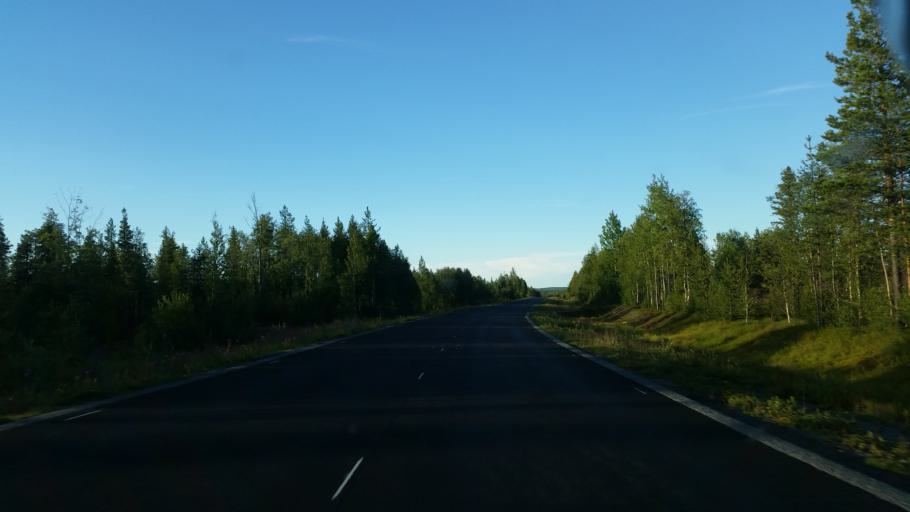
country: SE
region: Vaesterbotten
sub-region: Dorotea Kommun
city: Dorotea
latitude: 64.3200
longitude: 16.6131
